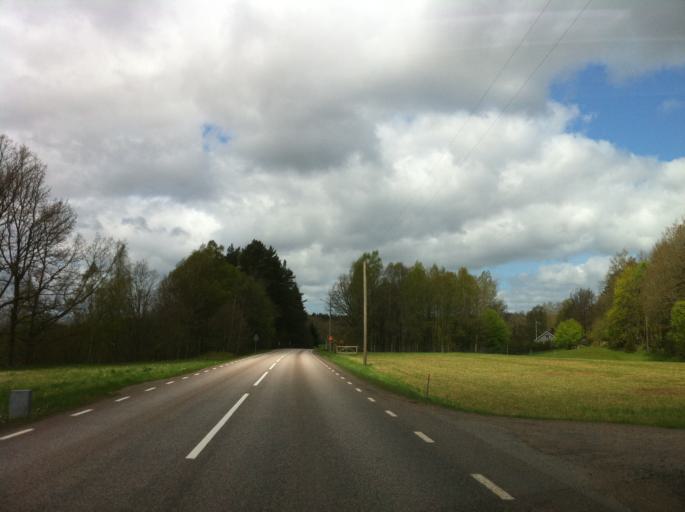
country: SE
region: Vaestra Goetaland
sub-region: Alingsas Kommun
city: Ingared
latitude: 57.8421
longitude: 12.5040
